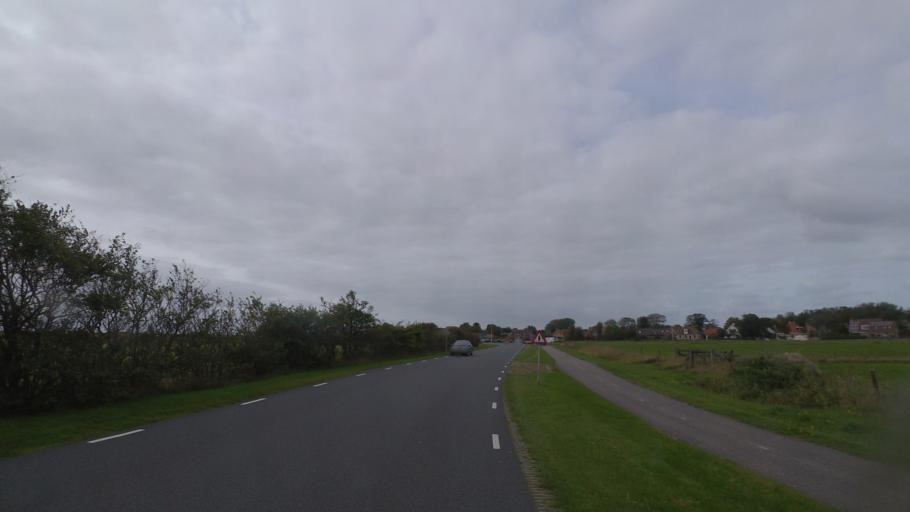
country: NL
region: Friesland
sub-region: Gemeente Ameland
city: Nes
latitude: 53.4419
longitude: 5.7777
